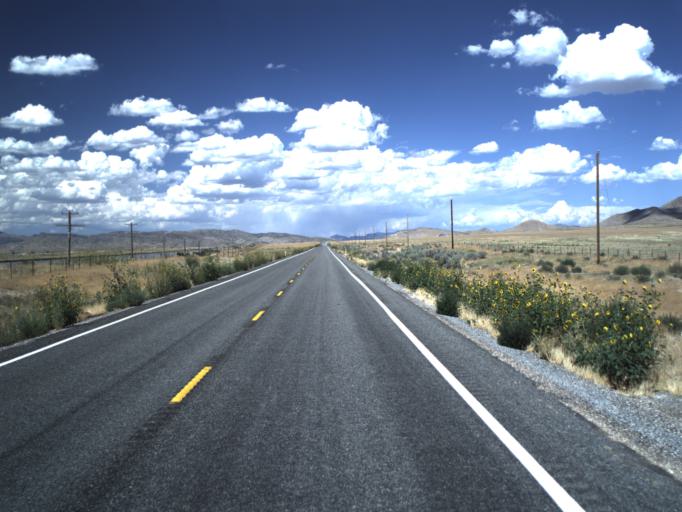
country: US
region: Utah
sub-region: Millard County
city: Delta
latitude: 39.5928
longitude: -112.3290
